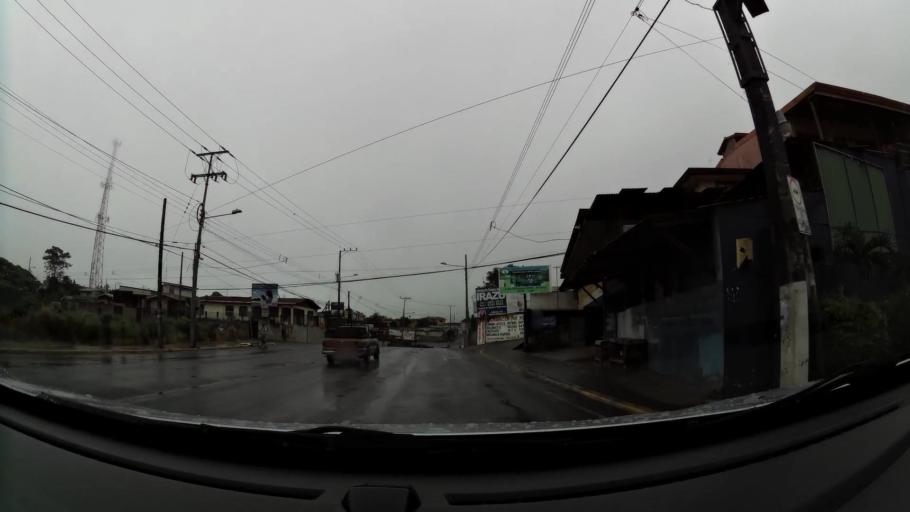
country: CR
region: Cartago
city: Paraiso
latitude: 9.8397
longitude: -83.8714
